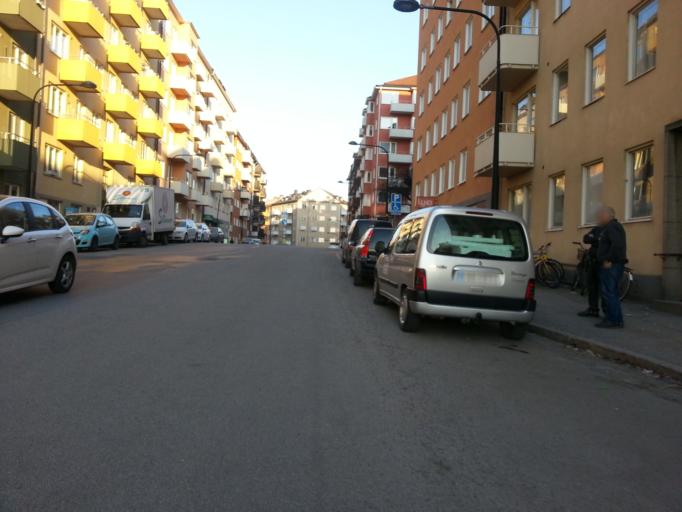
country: SE
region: Stockholm
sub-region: Solna Kommun
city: Solna
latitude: 59.3249
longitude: 18.0044
